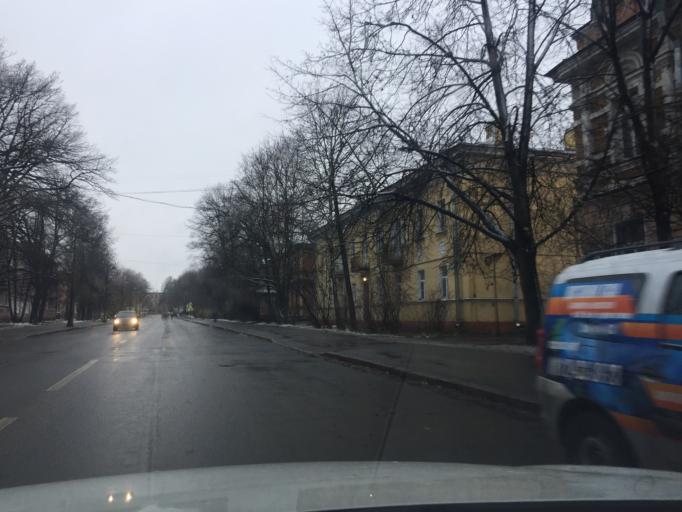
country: RU
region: St.-Petersburg
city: Pushkin
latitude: 59.7222
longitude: 30.4050
